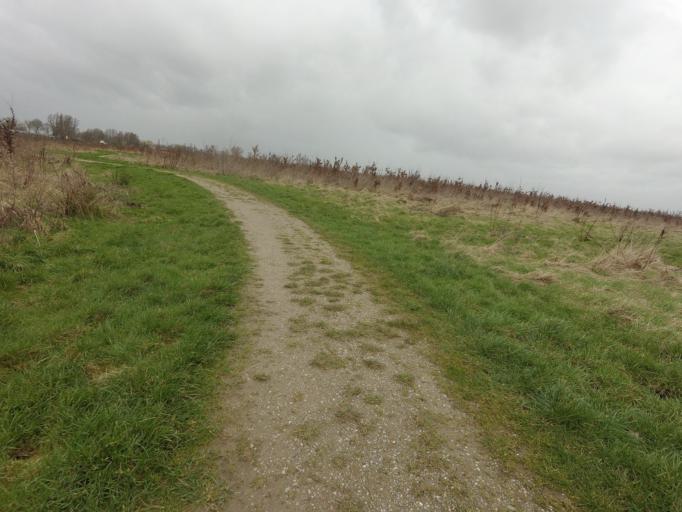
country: NL
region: Utrecht
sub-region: Gemeente IJsselstein
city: IJsselstein
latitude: 52.0434
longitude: 5.0314
